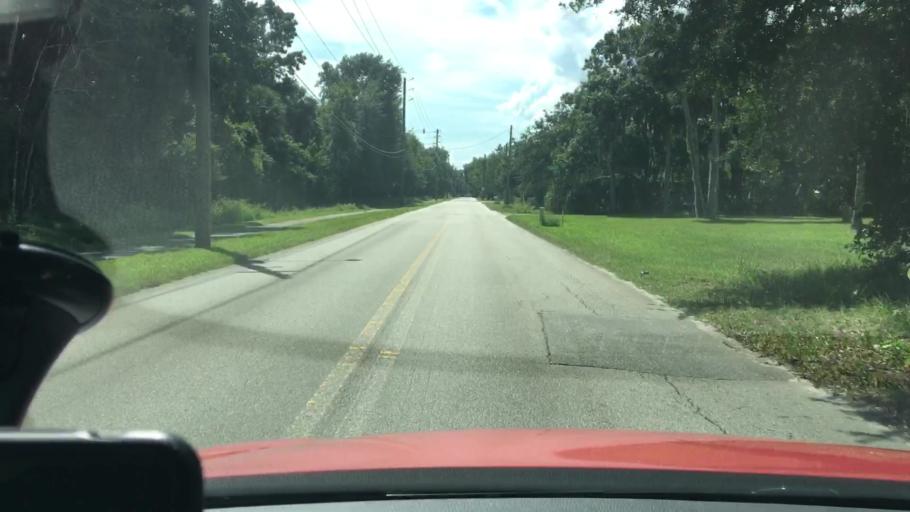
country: US
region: Florida
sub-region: Volusia County
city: New Smyrna Beach
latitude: 29.0142
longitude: -80.9269
